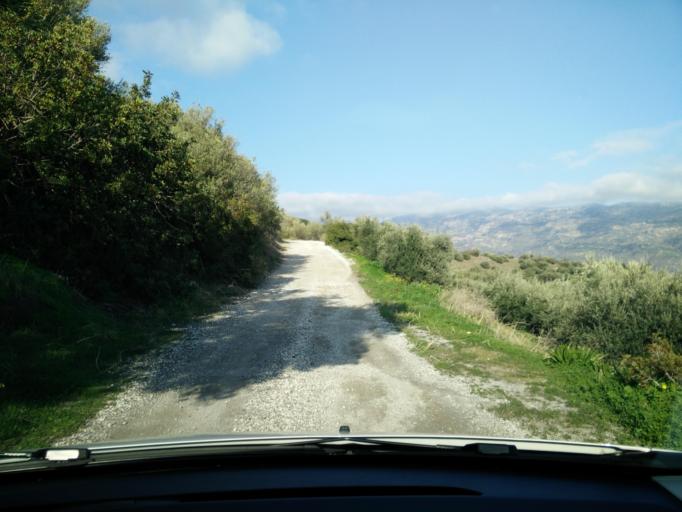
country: GR
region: Crete
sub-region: Nomos Lasithiou
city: Gra Liyia
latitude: 35.0299
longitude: 25.5669
